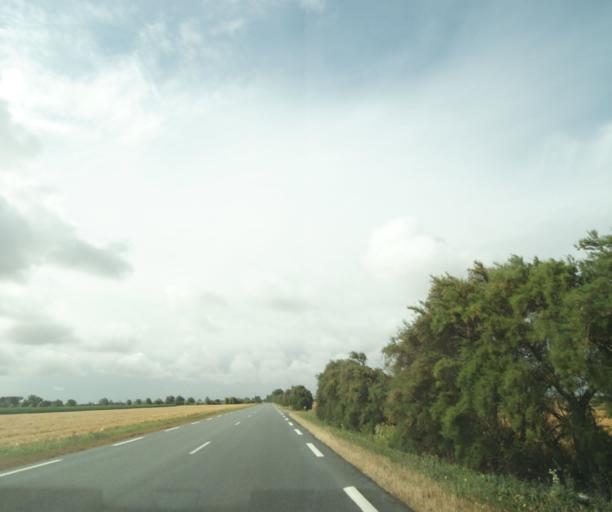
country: FR
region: Poitou-Charentes
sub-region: Departement de la Charente-Maritime
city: Andilly
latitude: 46.2666
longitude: -1.0675
